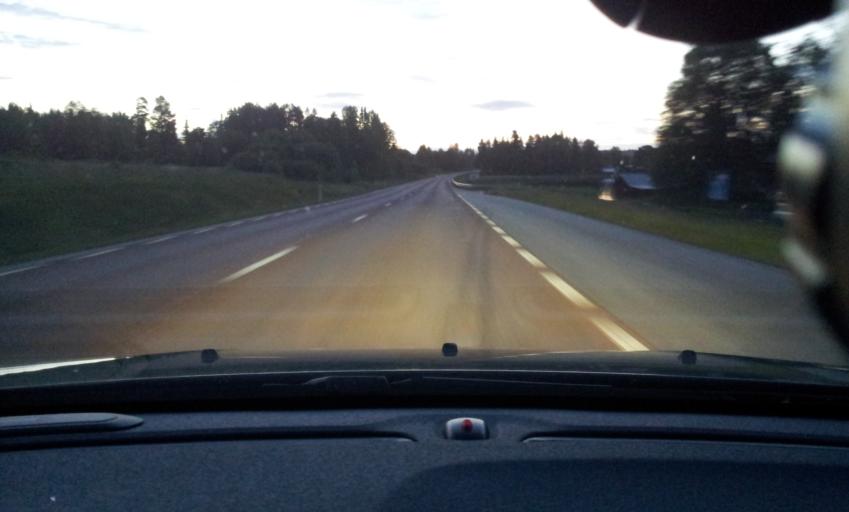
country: SE
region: Jaemtland
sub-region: Bergs Kommun
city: Hoverberg
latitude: 62.9605
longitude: 14.5542
